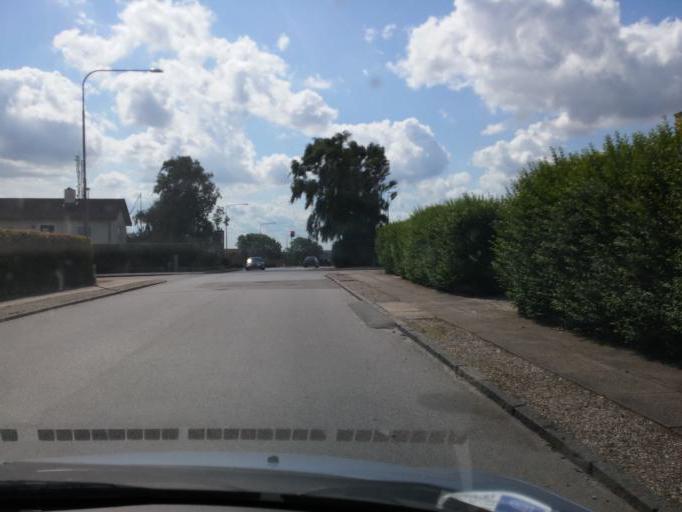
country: DK
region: South Denmark
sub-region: Kerteminde Kommune
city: Kerteminde
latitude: 55.4541
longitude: 10.6519
